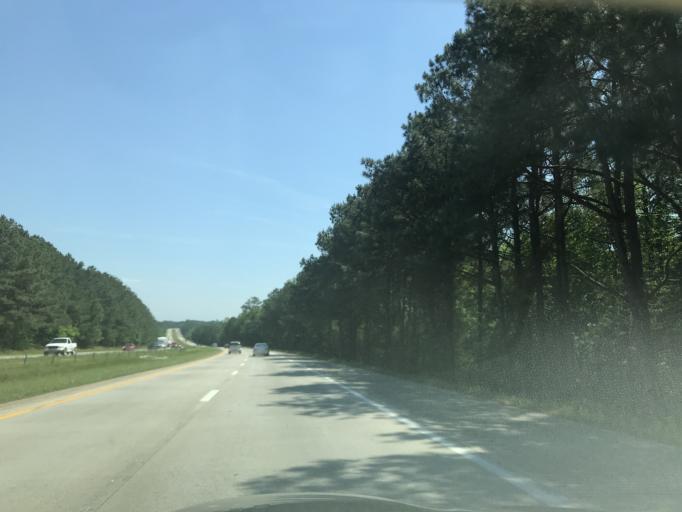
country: US
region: North Carolina
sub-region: Johnston County
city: Benson
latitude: 35.4682
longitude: -78.5477
